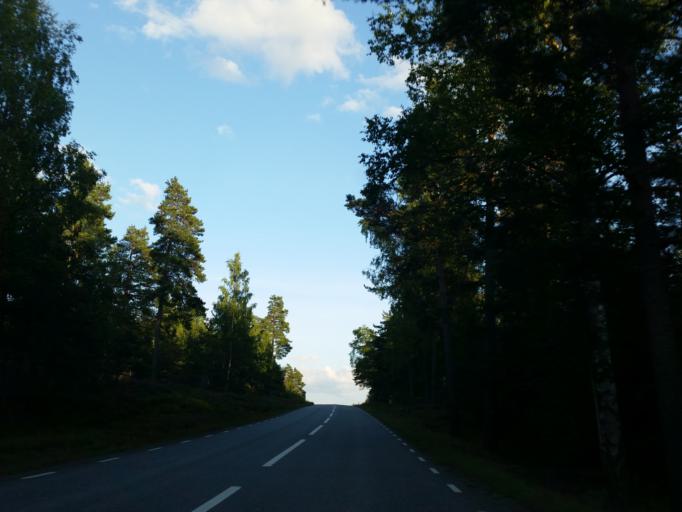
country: SE
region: Stockholm
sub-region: Sodertalje Kommun
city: Soedertaelje
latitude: 59.2323
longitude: 17.5494
